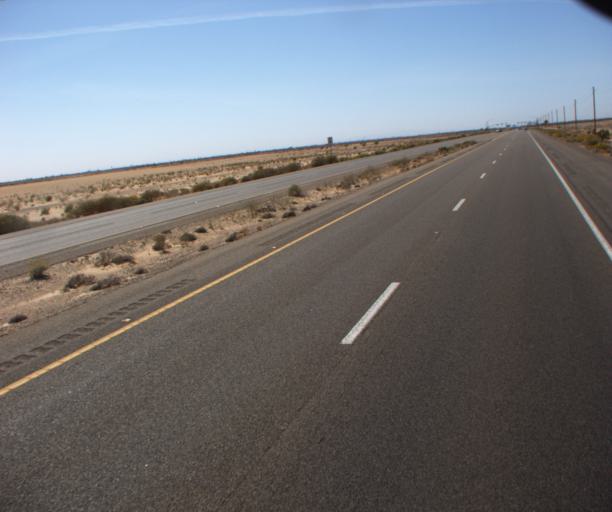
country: MX
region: Sonora
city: San Luis Rio Colorado
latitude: 32.4948
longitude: -114.6945
